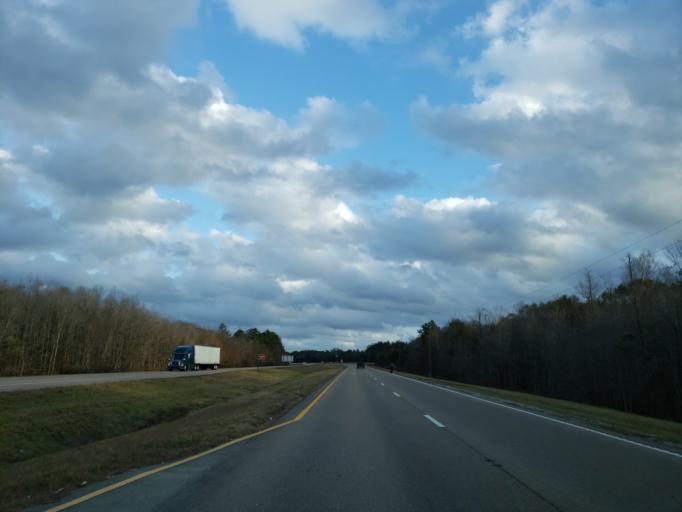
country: US
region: Mississippi
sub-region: Perry County
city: New Augusta
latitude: 31.1479
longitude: -88.8855
